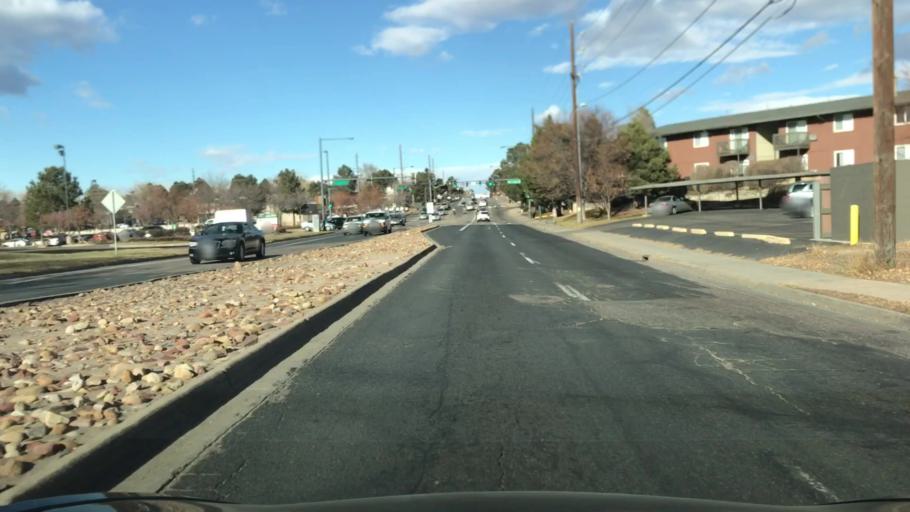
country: US
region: Colorado
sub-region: Arapahoe County
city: Glendale
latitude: 39.6964
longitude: -104.9035
